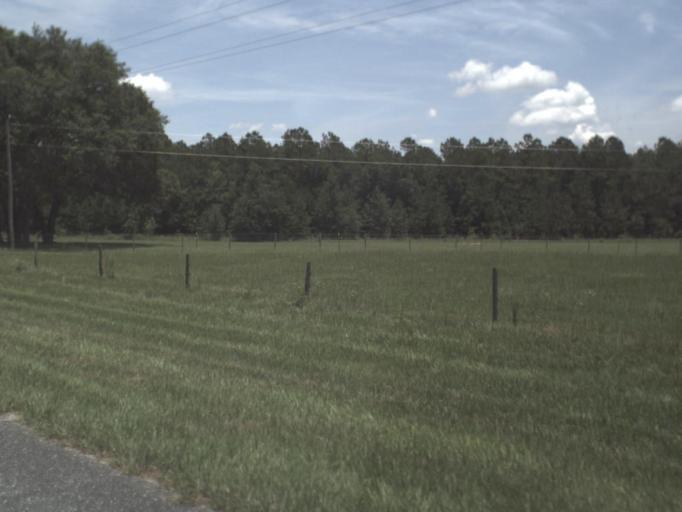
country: US
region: Florida
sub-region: Lafayette County
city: Mayo
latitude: 30.1912
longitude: -83.1203
